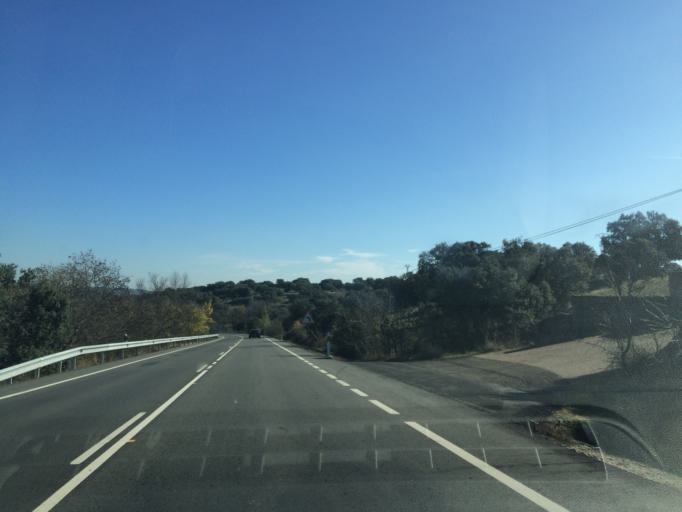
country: ES
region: Madrid
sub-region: Provincia de Madrid
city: Guadalix de la Sierra
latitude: 40.7811
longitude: -3.7188
